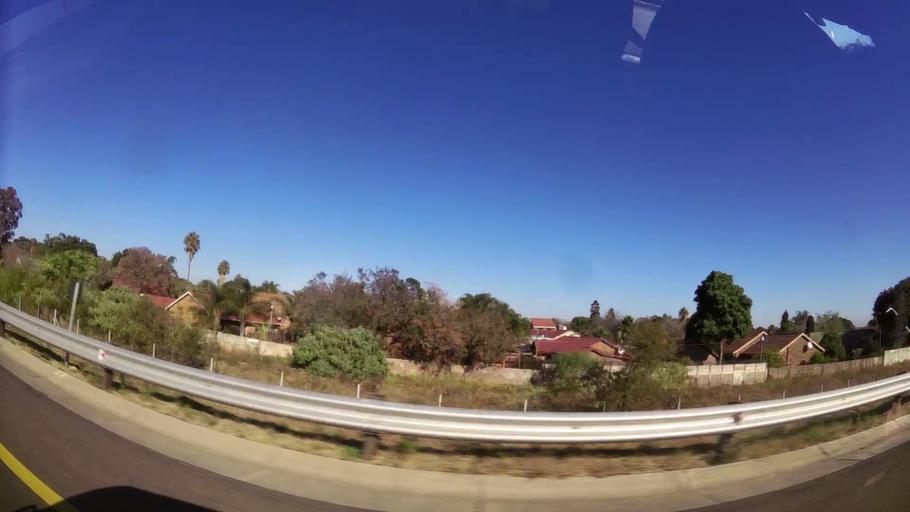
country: ZA
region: Gauteng
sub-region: City of Tshwane Metropolitan Municipality
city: Centurion
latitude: -25.8256
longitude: 28.2414
